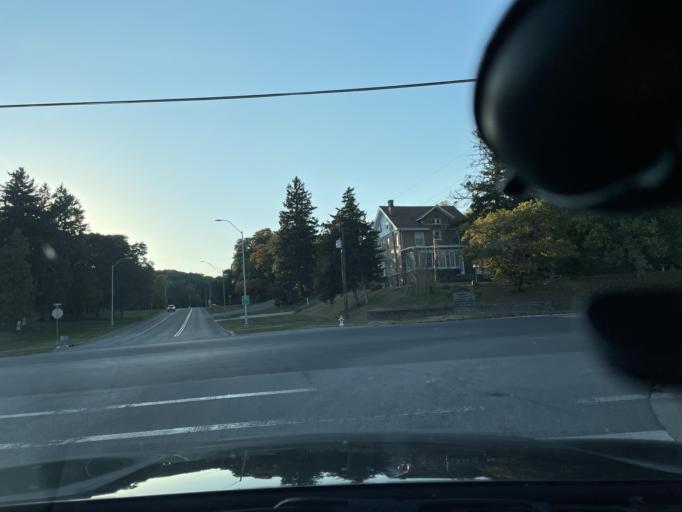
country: US
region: Missouri
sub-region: Buchanan County
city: Saint Joseph
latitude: 39.7991
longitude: -94.8446
